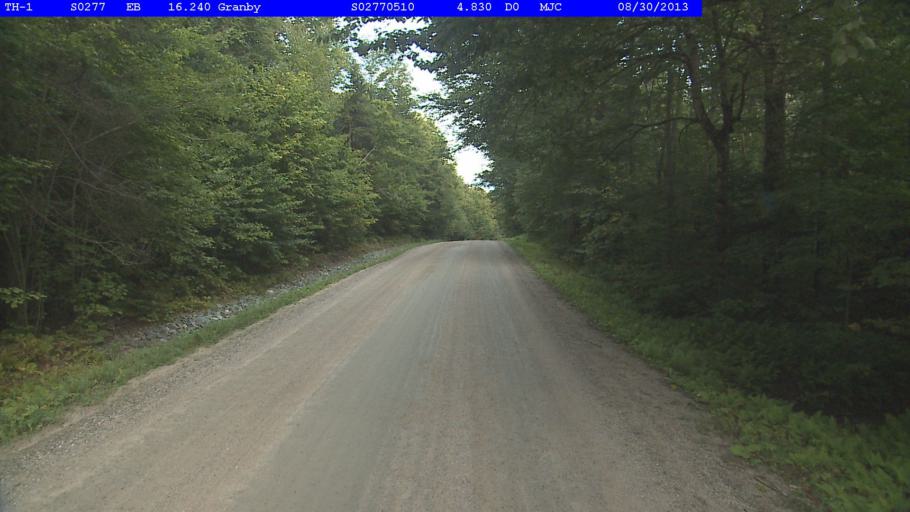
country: US
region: Vermont
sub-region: Essex County
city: Guildhall
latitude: 44.5779
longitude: -71.6769
